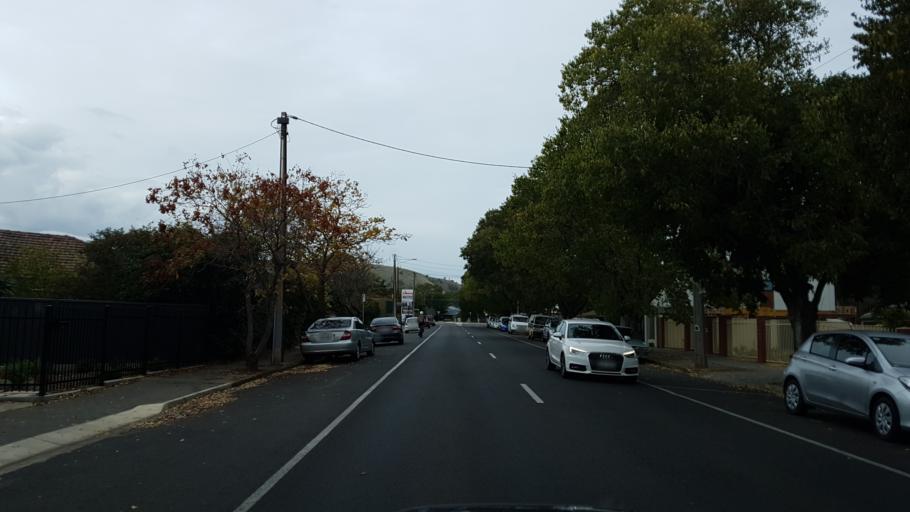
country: AU
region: South Australia
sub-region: Mitcham
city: Hawthorn
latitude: -34.9760
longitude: 138.6127
